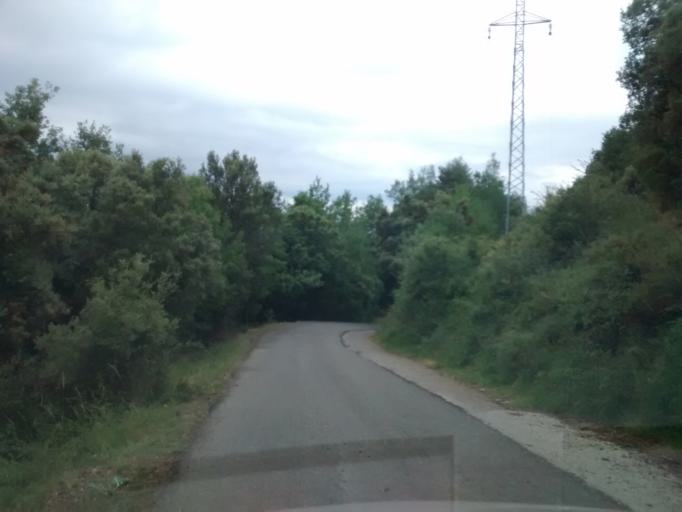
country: ES
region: Aragon
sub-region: Provincia de Huesca
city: Puertolas
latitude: 42.5320
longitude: 0.1304
